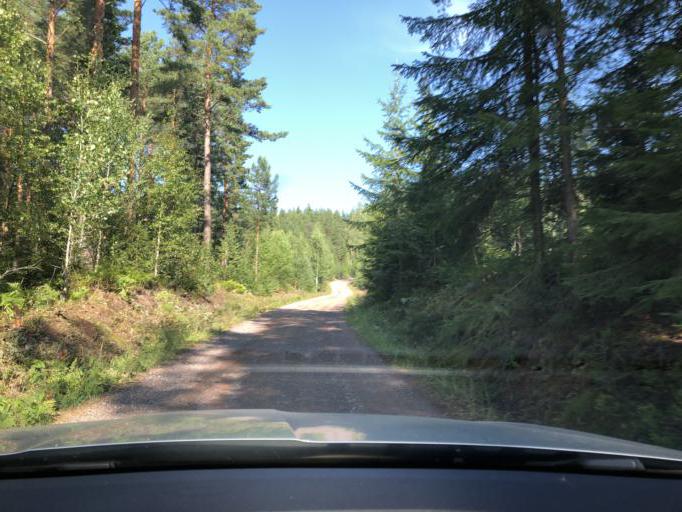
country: SE
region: Dalarna
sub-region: Hedemora Kommun
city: Hedemora
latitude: 60.3249
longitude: 15.8959
